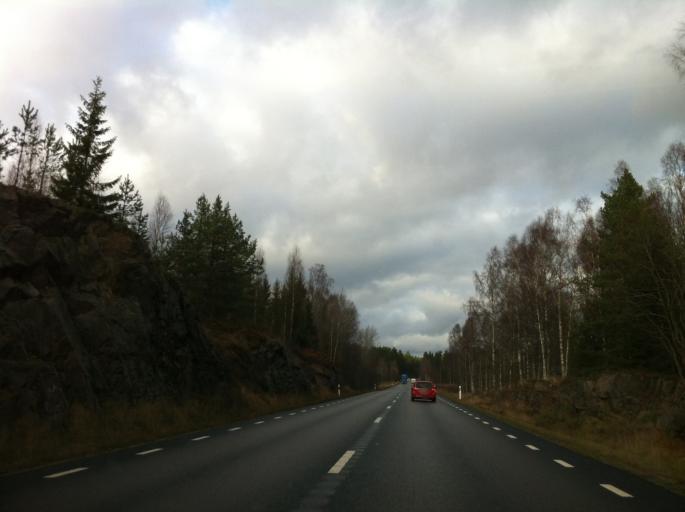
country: SE
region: Kalmar
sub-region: Hultsfreds Kommun
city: Hultsfred
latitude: 57.5340
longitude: 15.8187
